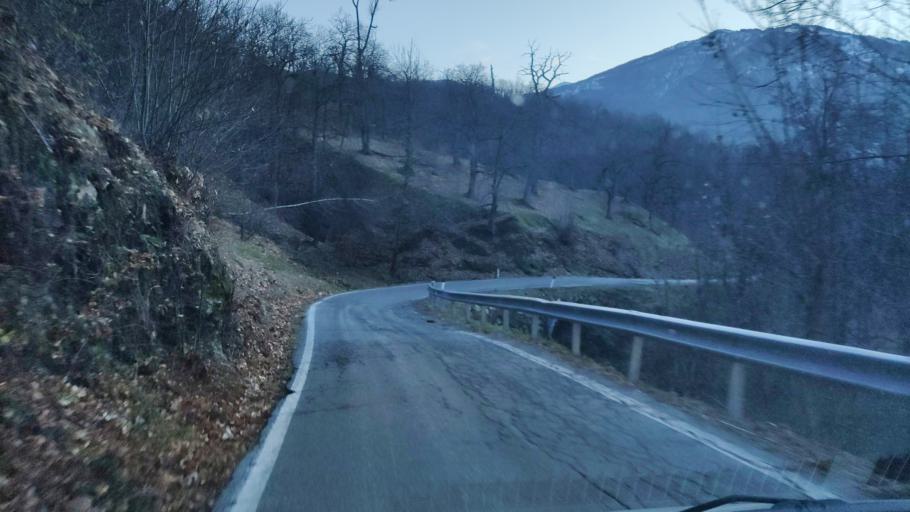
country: IT
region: Piedmont
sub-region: Provincia di Cuneo
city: Lisio
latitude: 44.2915
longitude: 7.9810
